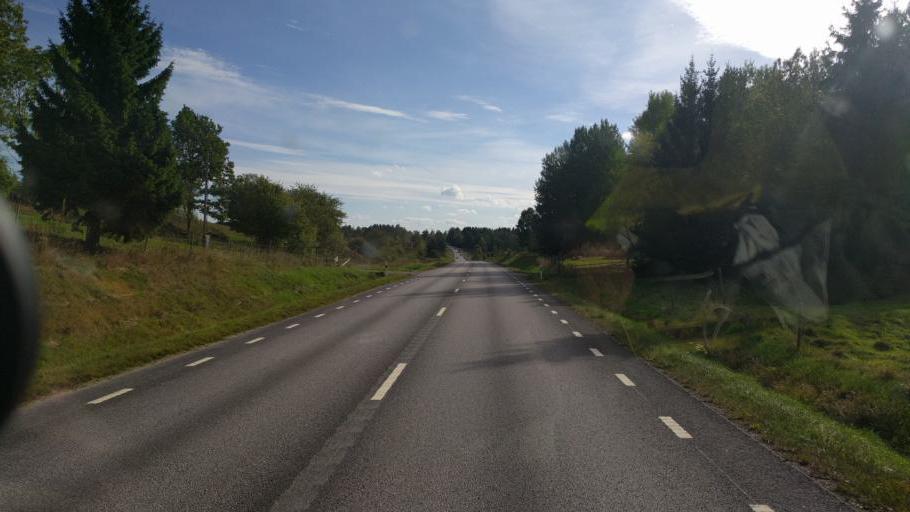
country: SE
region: OEstergoetland
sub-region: Kinda Kommun
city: Kisa
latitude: 57.9283
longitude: 15.6725
